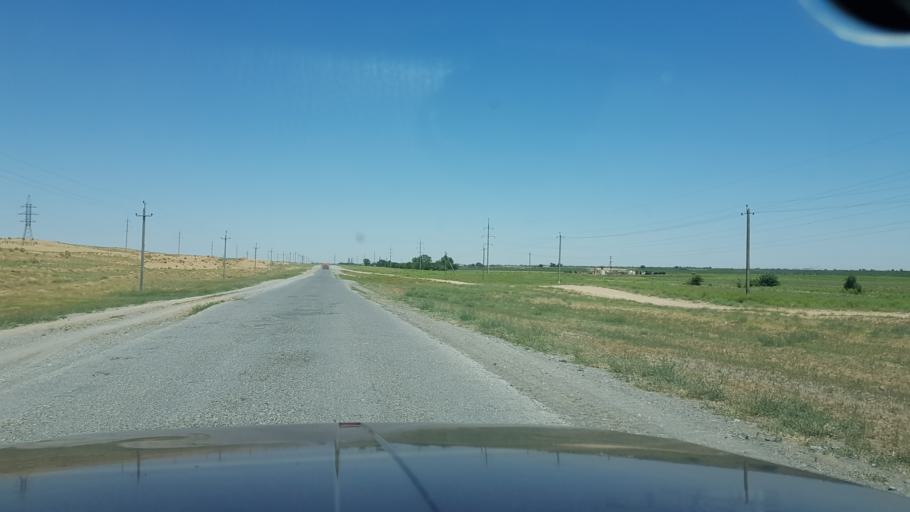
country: TM
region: Ahal
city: Annau
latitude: 37.8716
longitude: 58.7196
